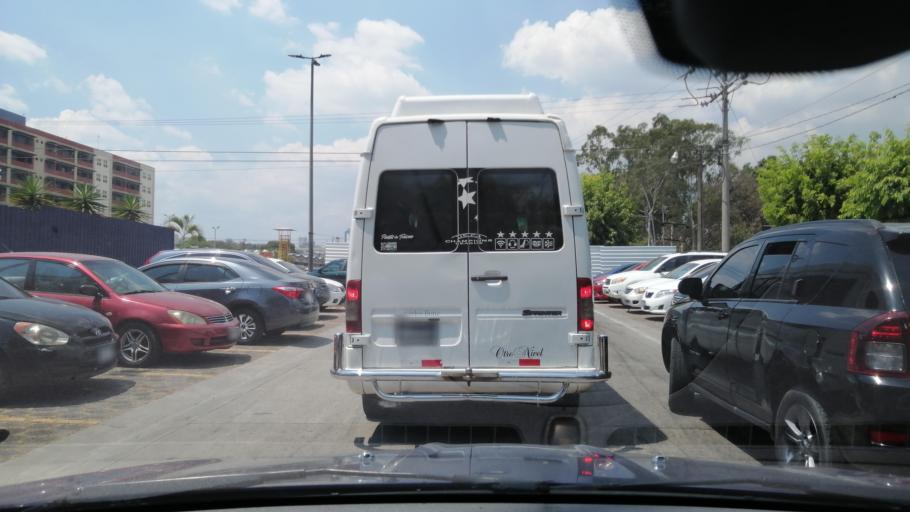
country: SV
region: San Salvador
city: San Salvador
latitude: 13.7041
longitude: -89.2024
